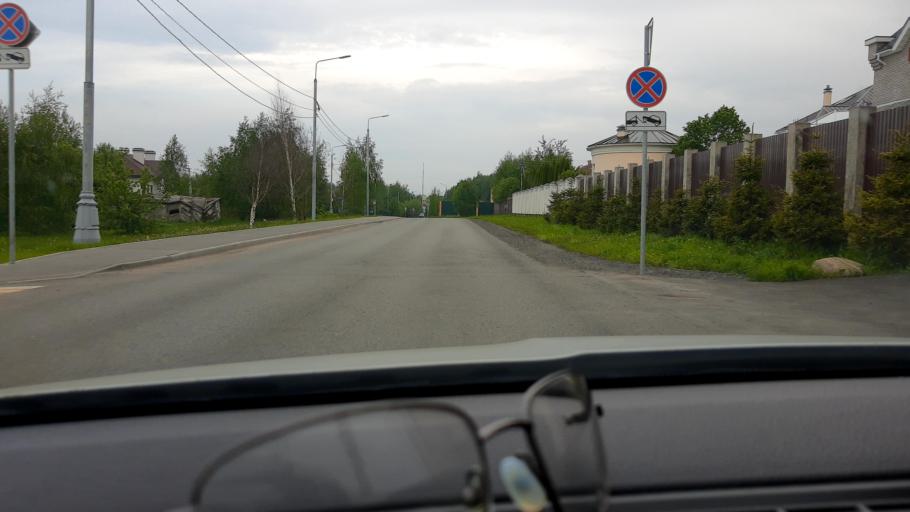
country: RU
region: Moskovskaya
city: Poselok Mar'ino
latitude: 55.5204
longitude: 37.3084
